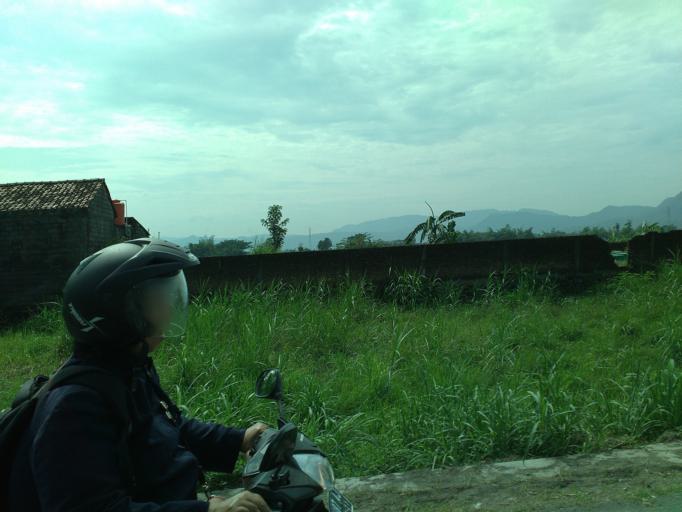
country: ID
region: Central Java
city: Candi Prambanan
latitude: -7.7504
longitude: 110.5204
